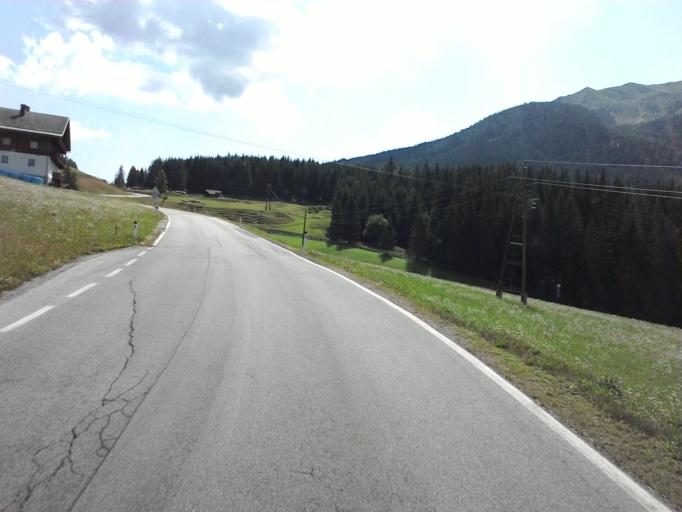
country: AT
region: Tyrol
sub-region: Politischer Bezirk Lienz
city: Kartitsch
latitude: 46.7199
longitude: 12.5214
